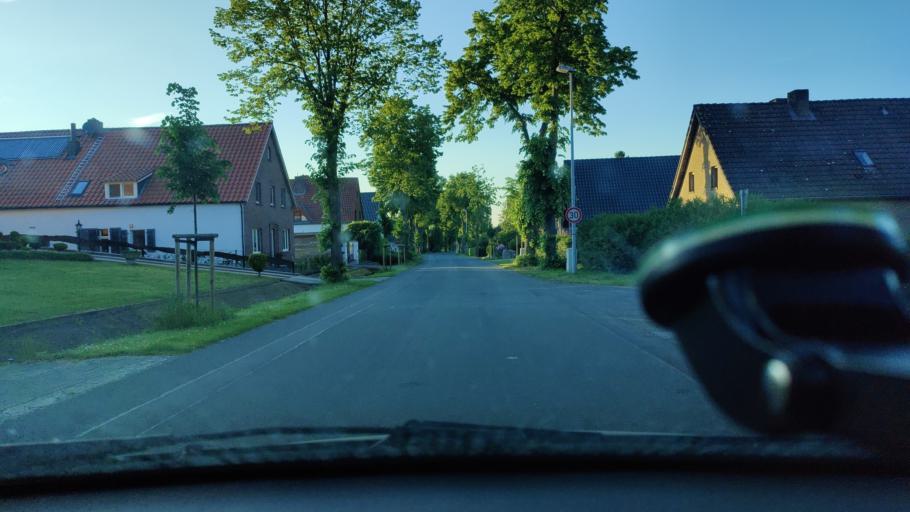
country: DE
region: North Rhine-Westphalia
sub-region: Regierungsbezirk Dusseldorf
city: Kranenburg
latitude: 51.7675
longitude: 6.0241
